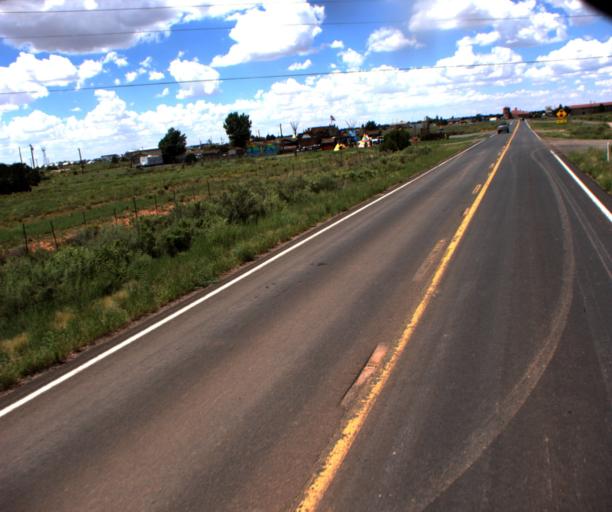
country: US
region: Arizona
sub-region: Coconino County
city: Grand Canyon Village
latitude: 35.6489
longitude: -112.1348
